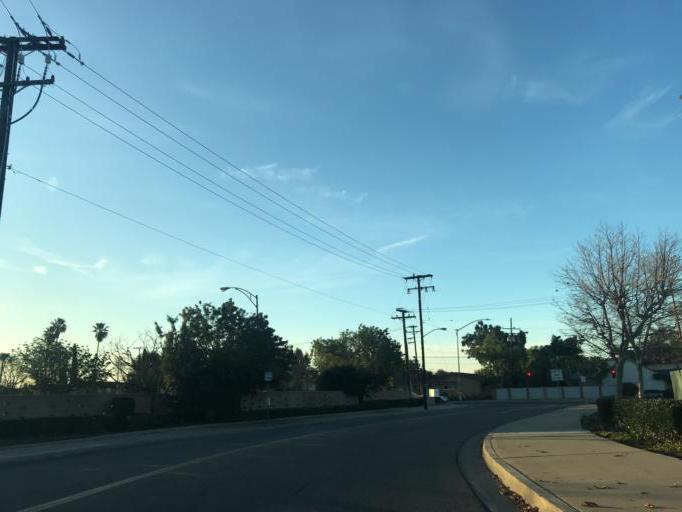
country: US
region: California
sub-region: Orange County
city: Villa Park
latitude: 33.8238
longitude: -117.8395
